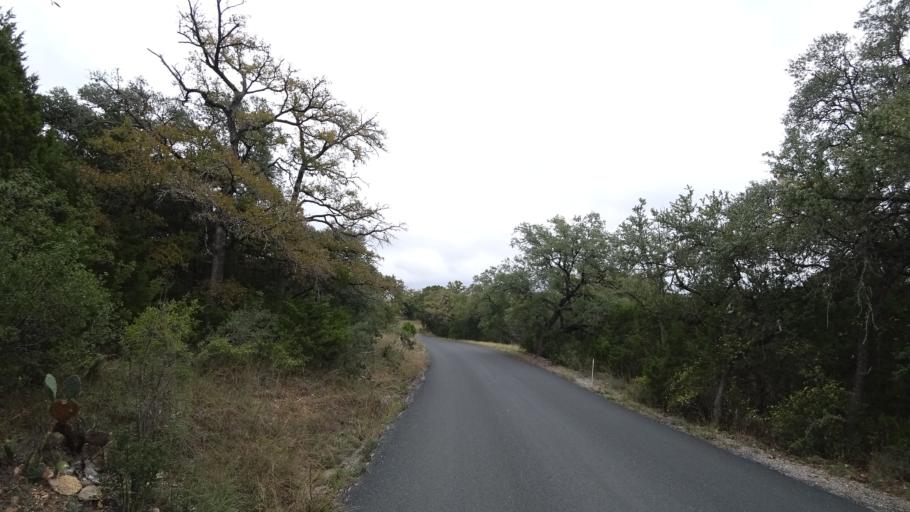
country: US
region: Texas
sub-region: Travis County
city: Bee Cave
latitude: 30.3445
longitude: -97.9332
